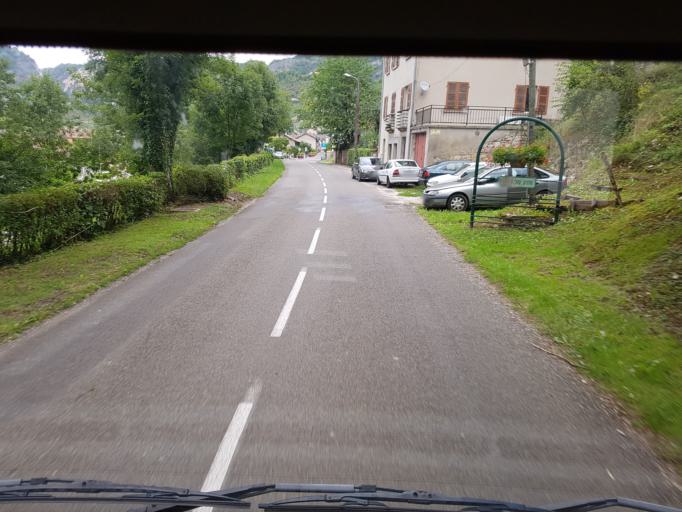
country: FR
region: Rhone-Alpes
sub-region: Departement de l'Ain
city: Poncin
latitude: 46.0778
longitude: 5.4597
